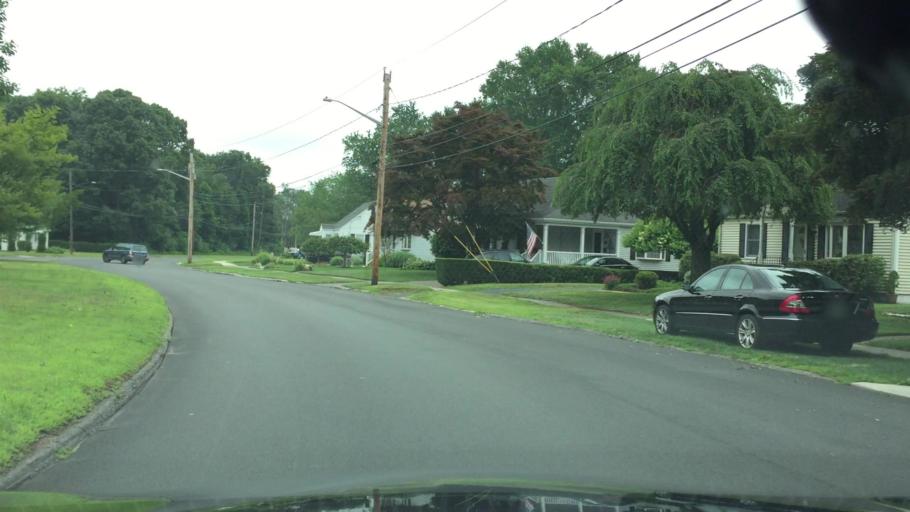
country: US
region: Connecticut
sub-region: New Haven County
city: City of Milford (balance)
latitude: 41.2142
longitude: -73.0680
